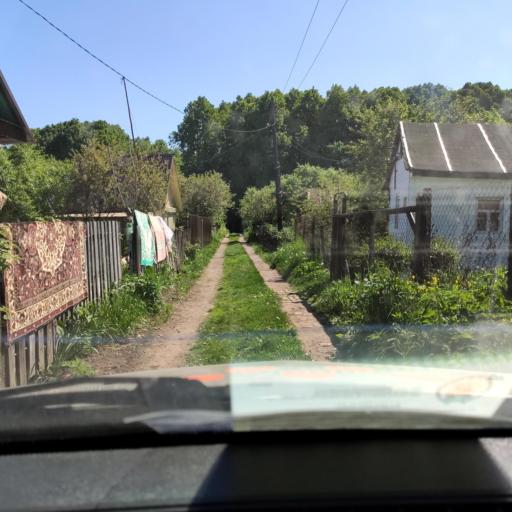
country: RU
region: Bashkortostan
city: Blagoveshchensk
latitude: 54.9414
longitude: 56.0851
